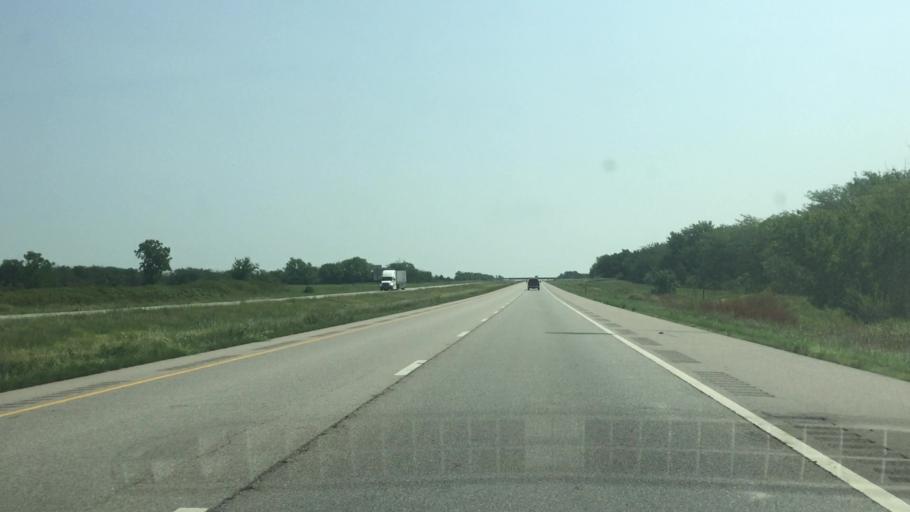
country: US
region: Kansas
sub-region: Lyon County
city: Emporia
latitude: 38.4099
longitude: -95.9647
